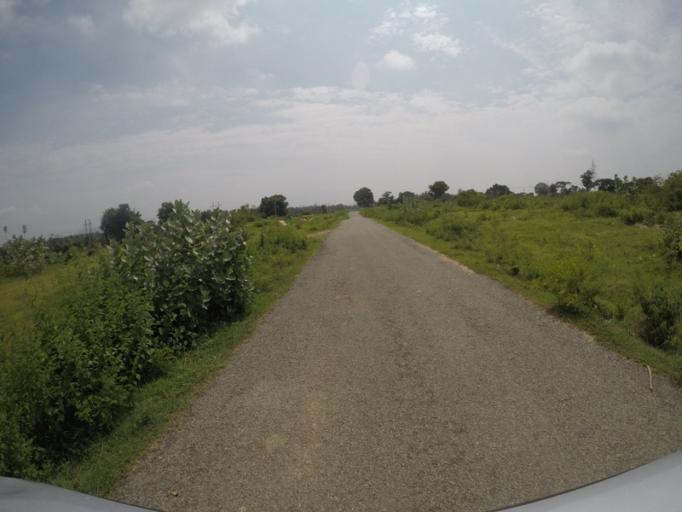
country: IN
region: Karnataka
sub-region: Ramanagara
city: Kanakapura
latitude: 12.4602
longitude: 77.3301
